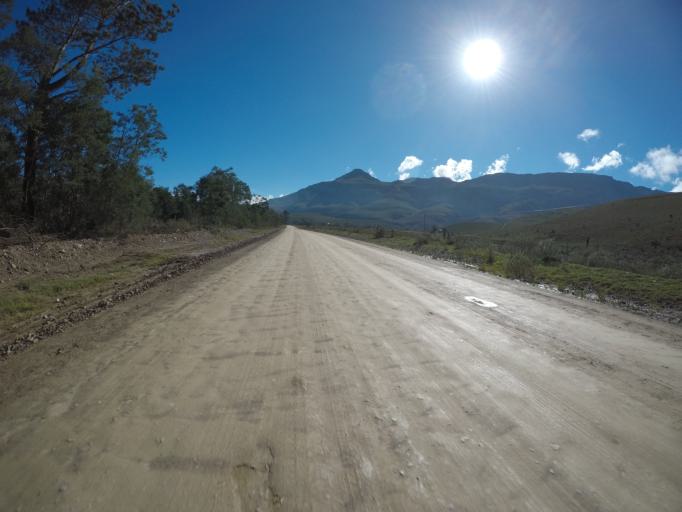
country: ZA
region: Western Cape
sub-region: Overberg District Municipality
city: Caledon
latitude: -34.0585
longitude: 19.6211
